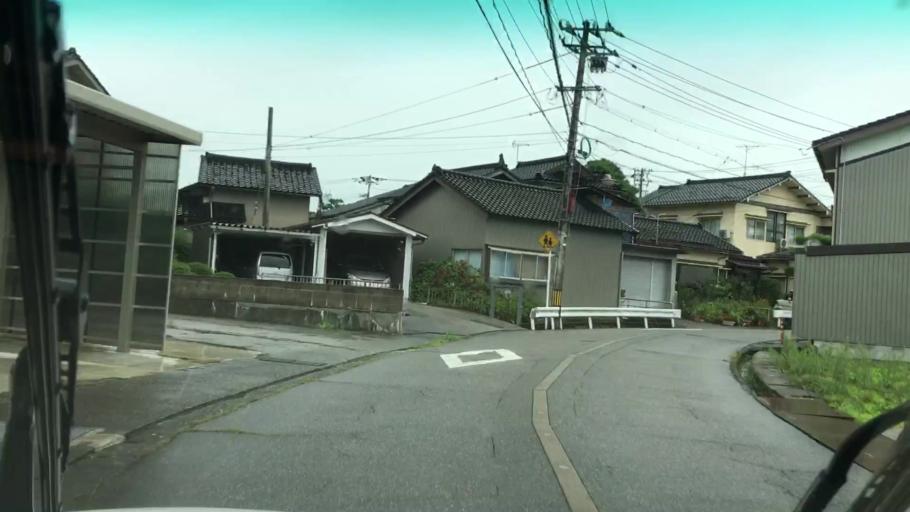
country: JP
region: Toyama
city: Kamiichi
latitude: 36.6574
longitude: 137.3185
